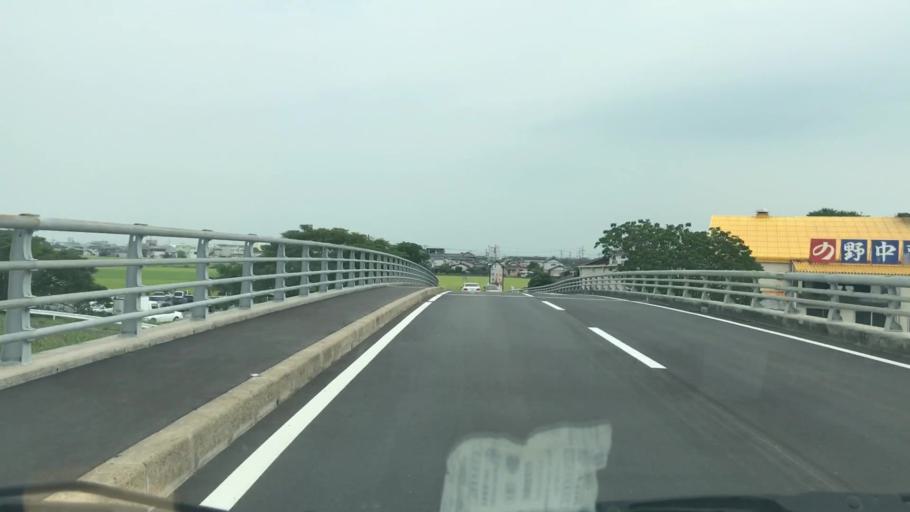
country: JP
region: Saga Prefecture
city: Saga-shi
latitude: 33.2274
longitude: 130.2652
